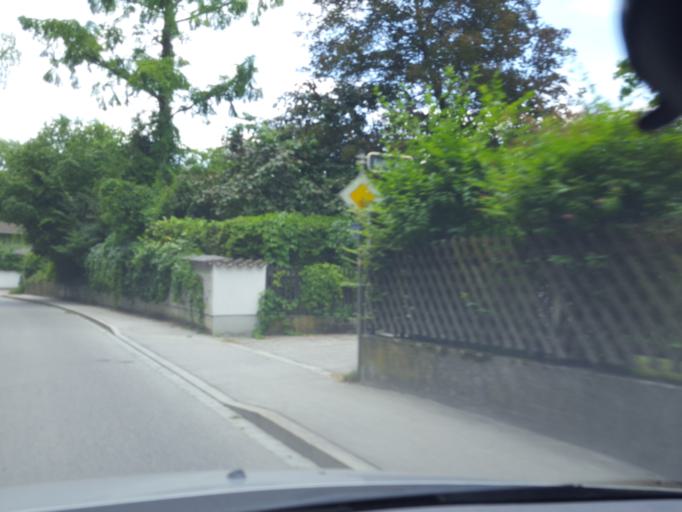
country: DE
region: Bavaria
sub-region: Lower Bavaria
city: Vilsbiburg
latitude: 48.4508
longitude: 12.3684
